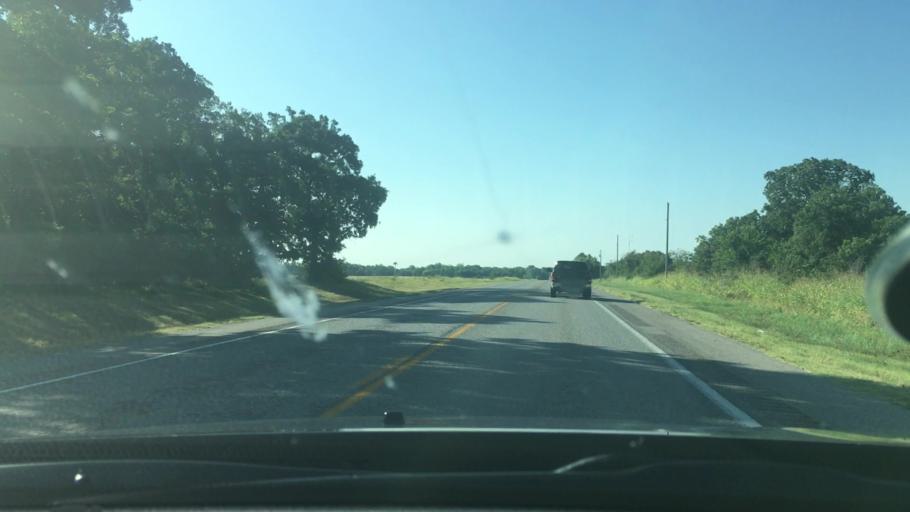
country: US
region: Oklahoma
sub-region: Johnston County
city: Tishomingo
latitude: 34.2588
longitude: -96.7675
